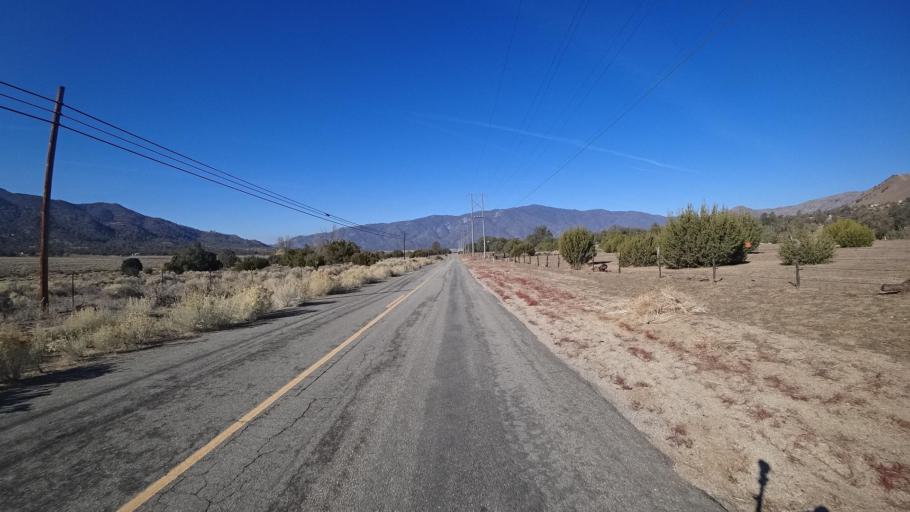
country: US
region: California
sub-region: Kern County
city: Bodfish
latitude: 35.4016
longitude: -118.4754
